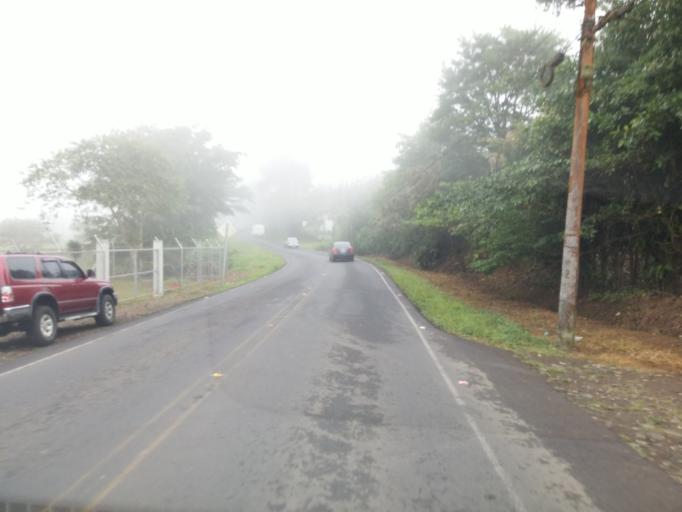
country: CR
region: Alajuela
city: San Ramon
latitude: 10.1734
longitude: -84.4984
